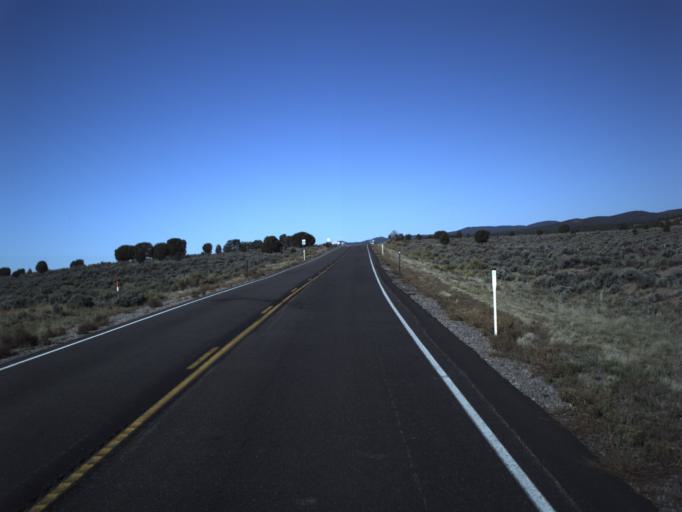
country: US
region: Utah
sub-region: Washington County
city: Enterprise
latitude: 37.7238
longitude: -114.0464
